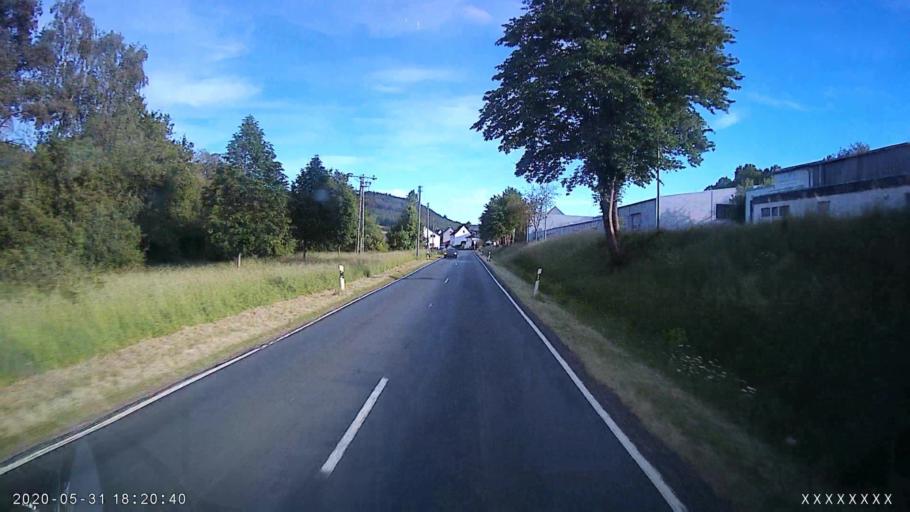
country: DE
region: Hesse
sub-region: Regierungsbezirk Giessen
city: Haiger
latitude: 50.7762
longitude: 8.2070
